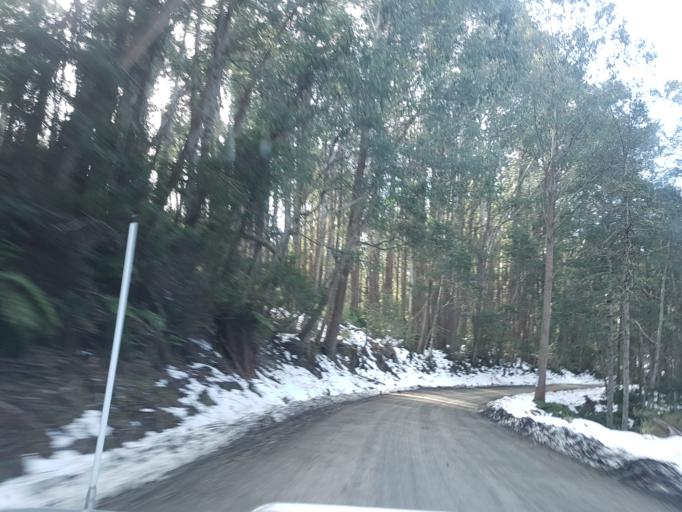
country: AU
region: Victoria
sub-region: Latrobe
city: Moe
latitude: -37.8306
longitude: 146.3388
